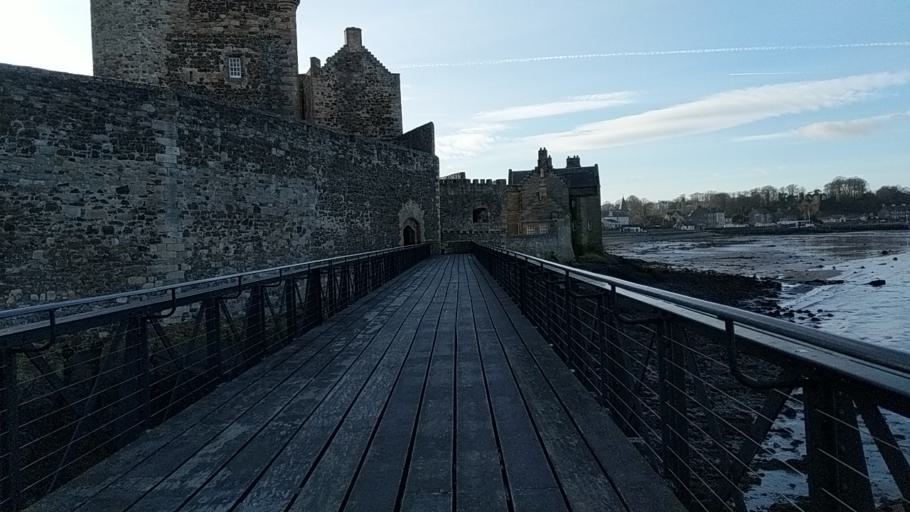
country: GB
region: Scotland
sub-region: Fife
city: Crossford
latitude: 56.0065
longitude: -3.5159
